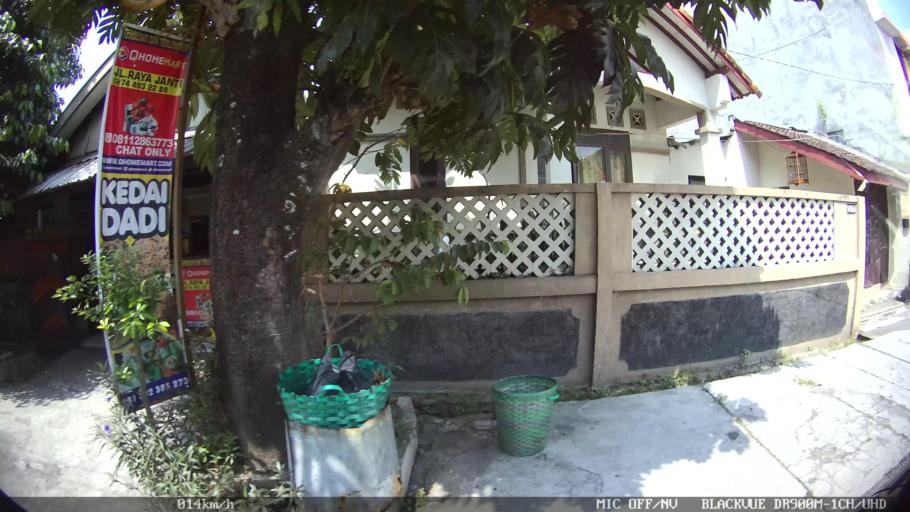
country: ID
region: Daerah Istimewa Yogyakarta
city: Depok
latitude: -7.7941
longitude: 110.4083
